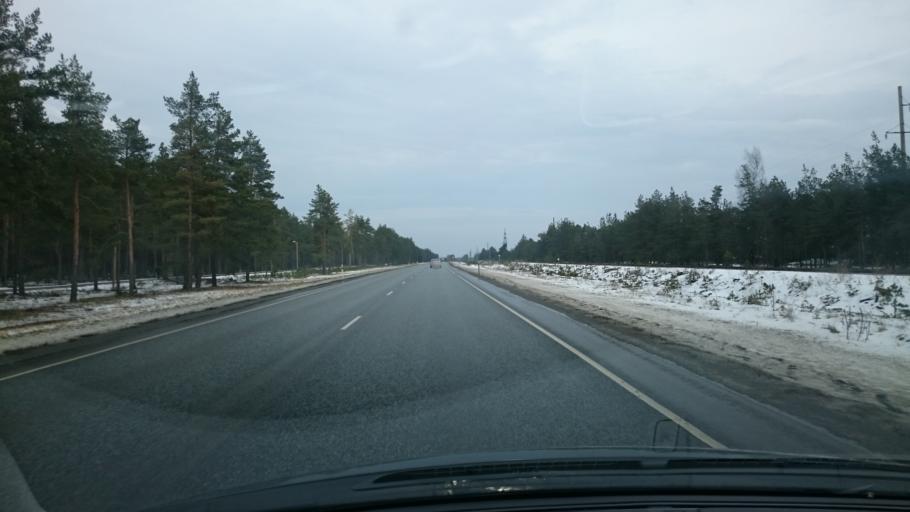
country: EE
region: Harju
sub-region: Saku vald
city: Saku
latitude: 59.3521
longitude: 24.7099
